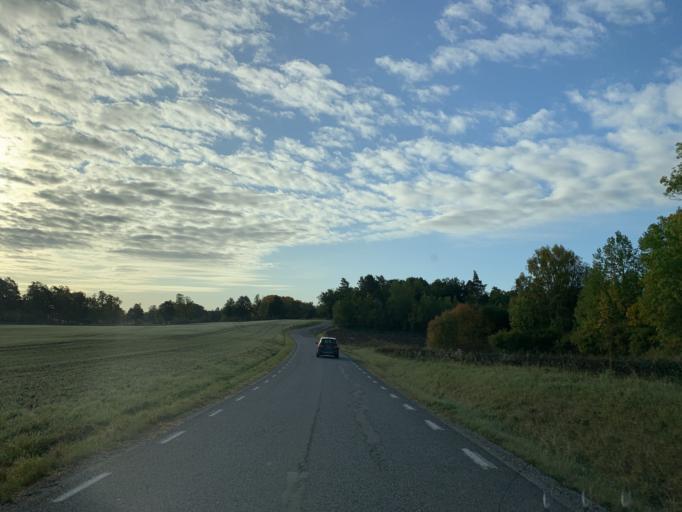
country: SE
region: Stockholm
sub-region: Upplands-Bro Kommun
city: Bro
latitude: 59.5021
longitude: 17.5877
